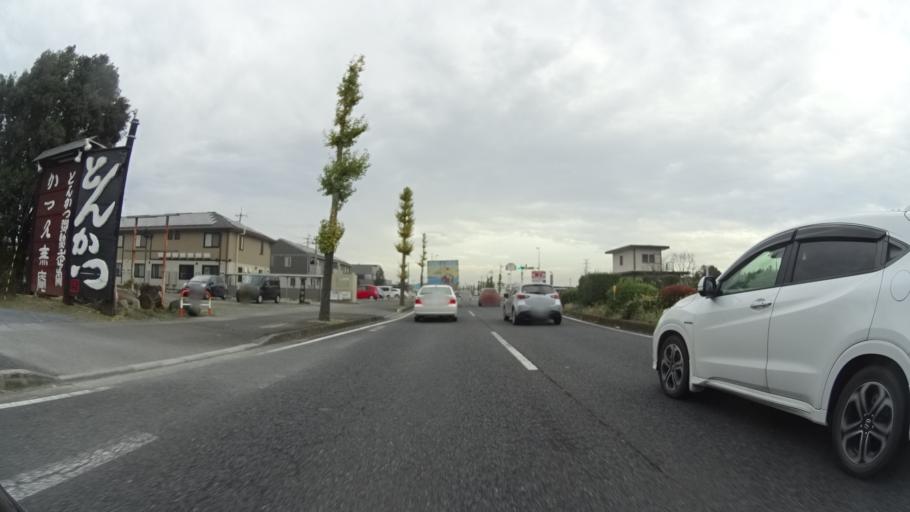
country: JP
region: Gunma
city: Maebashi-shi
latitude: 36.3759
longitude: 139.1194
